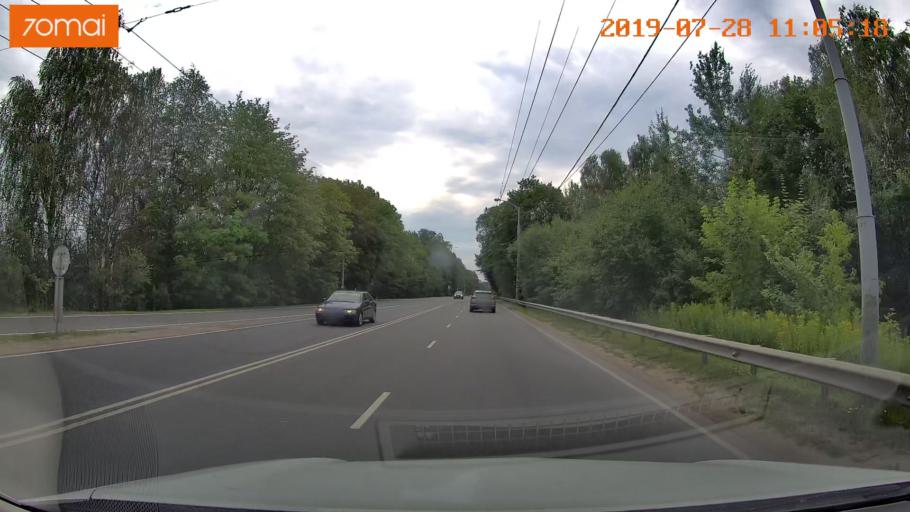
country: RU
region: Kaliningrad
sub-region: Gorod Kaliningrad
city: Kaliningrad
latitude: 54.7187
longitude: 20.3902
